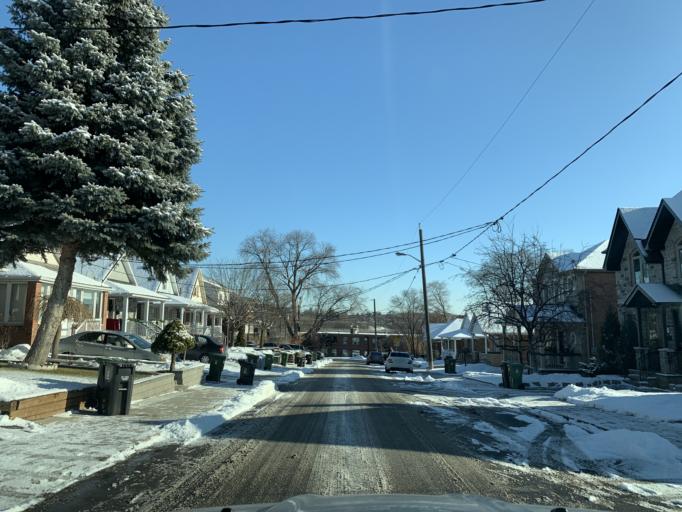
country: CA
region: Ontario
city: Toronto
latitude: 43.6832
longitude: -79.4845
